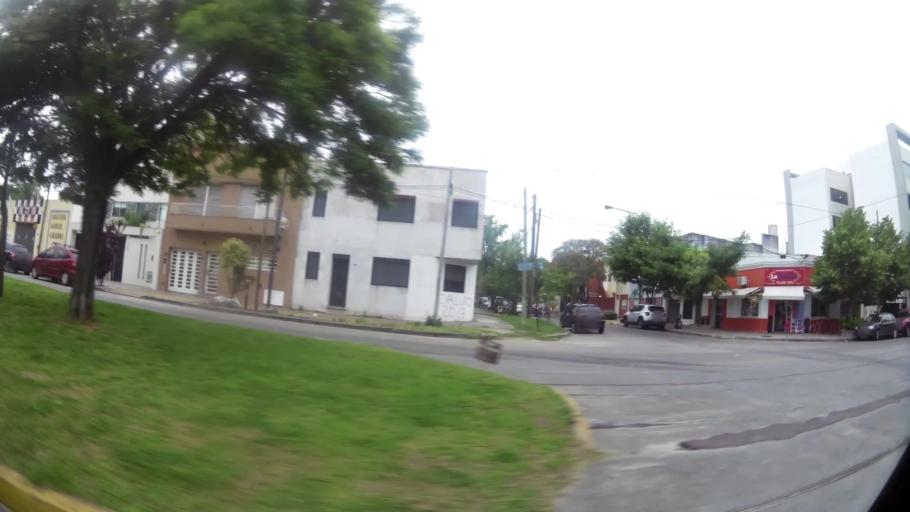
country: AR
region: Buenos Aires
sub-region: Partido de La Plata
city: La Plata
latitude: -34.9179
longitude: -57.9753
